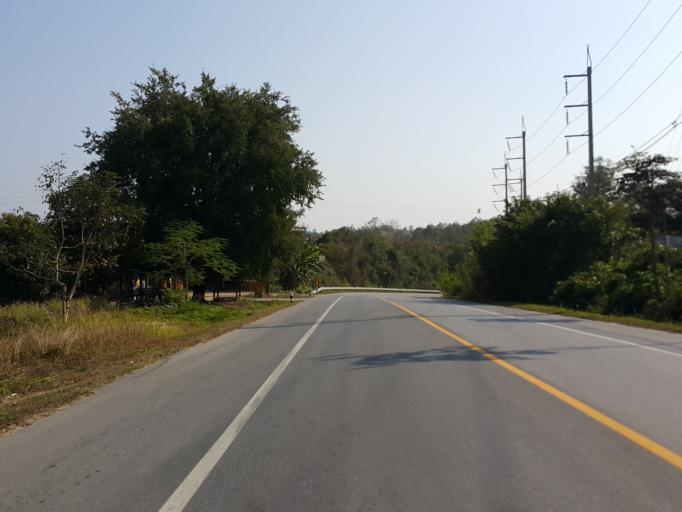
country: TH
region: Lampang
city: Chae Hom
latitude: 18.6230
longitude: 99.5444
